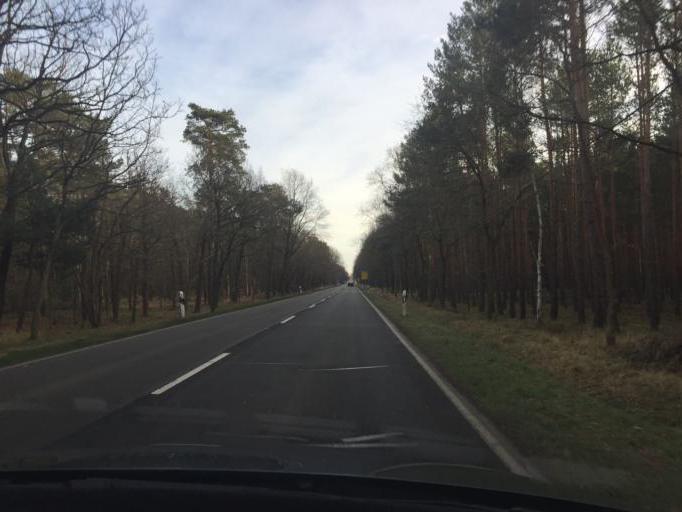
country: DE
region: Brandenburg
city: Cottbus
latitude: 51.7417
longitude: 14.3956
